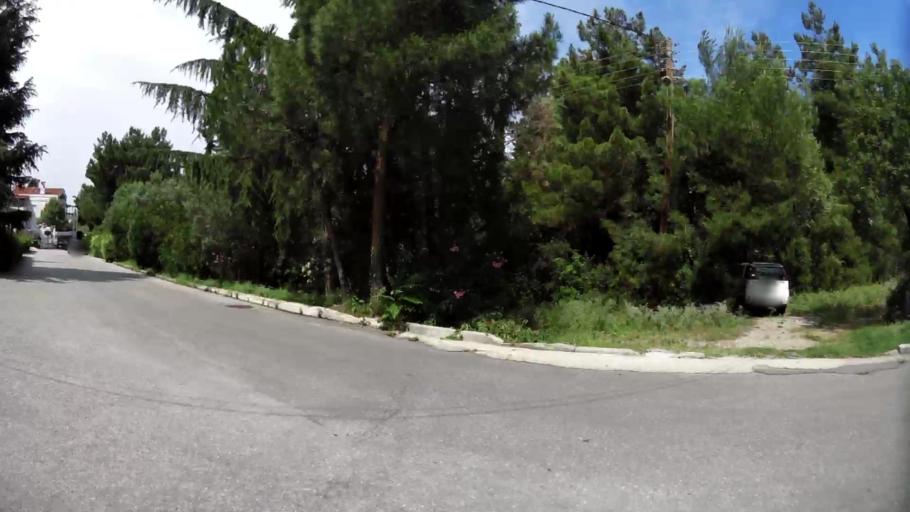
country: GR
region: Central Macedonia
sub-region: Nomos Thessalonikis
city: Panorama
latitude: 40.5890
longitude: 23.0182
